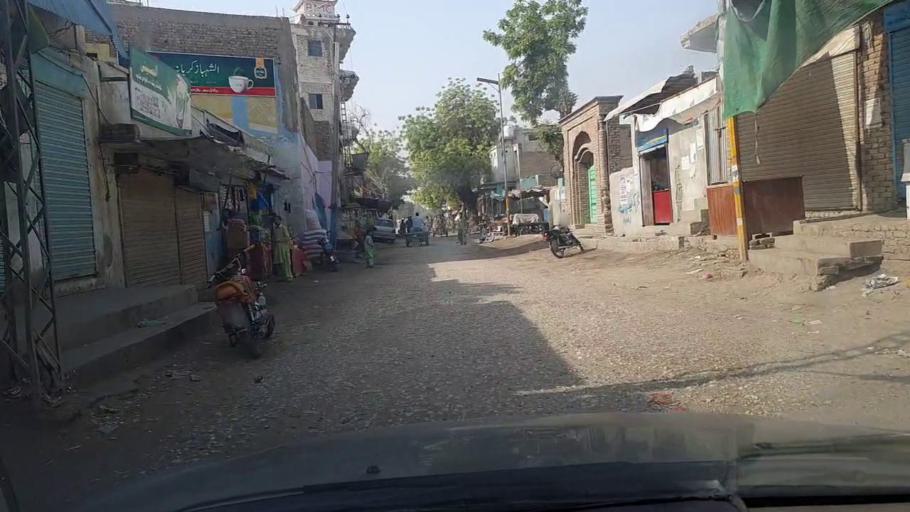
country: PK
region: Sindh
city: Mirpur Mathelo
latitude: 28.0203
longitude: 69.5513
